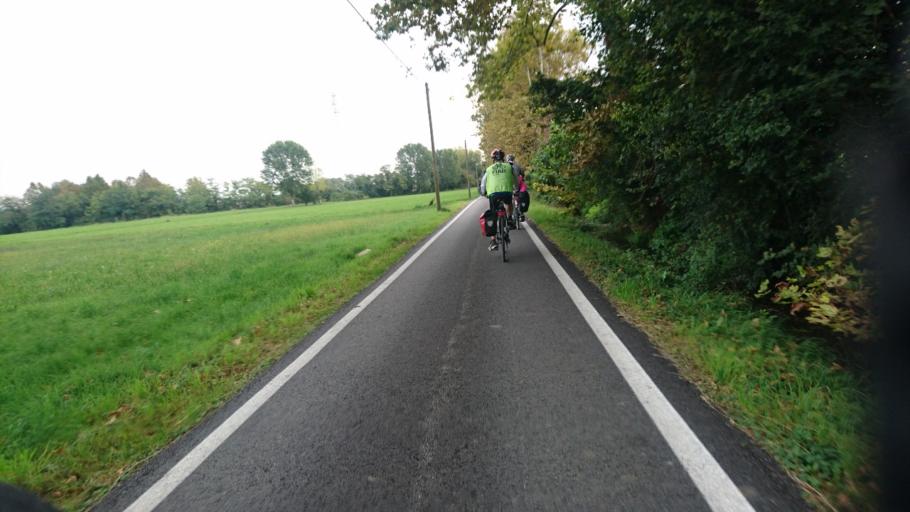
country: IT
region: Veneto
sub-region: Provincia di Verona
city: San Martino Buon Albergo
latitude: 45.4104
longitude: 11.1033
